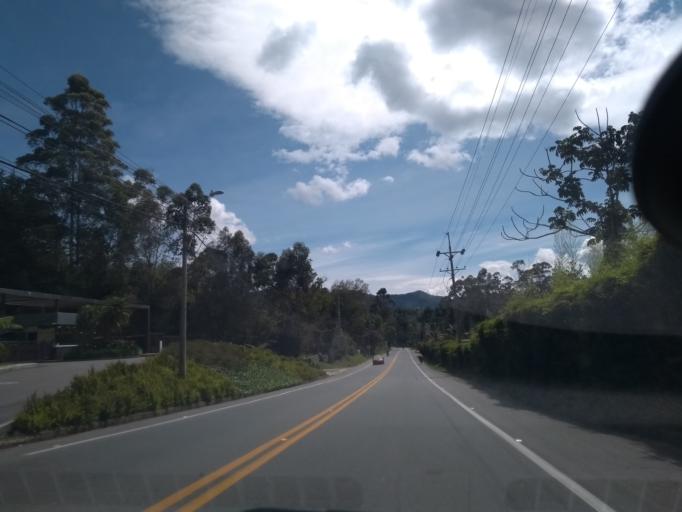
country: CO
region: Antioquia
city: Carmen de Viboral
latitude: 6.0953
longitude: -75.3829
